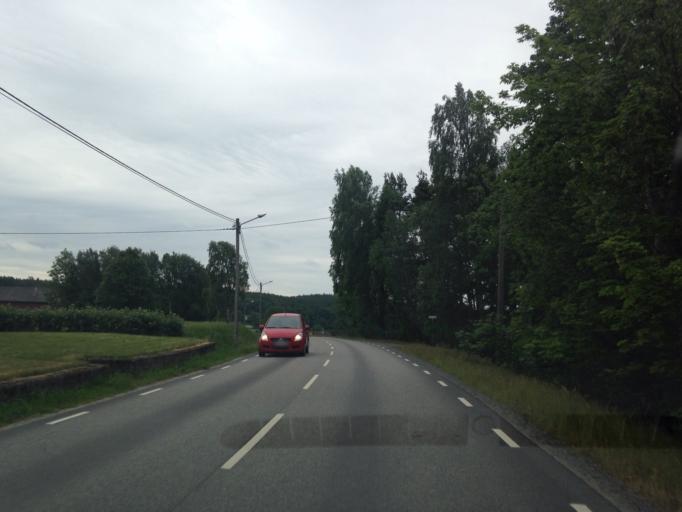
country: SE
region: Vaestra Goetaland
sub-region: Marks Kommun
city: Bua
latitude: 57.5074
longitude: 12.5475
